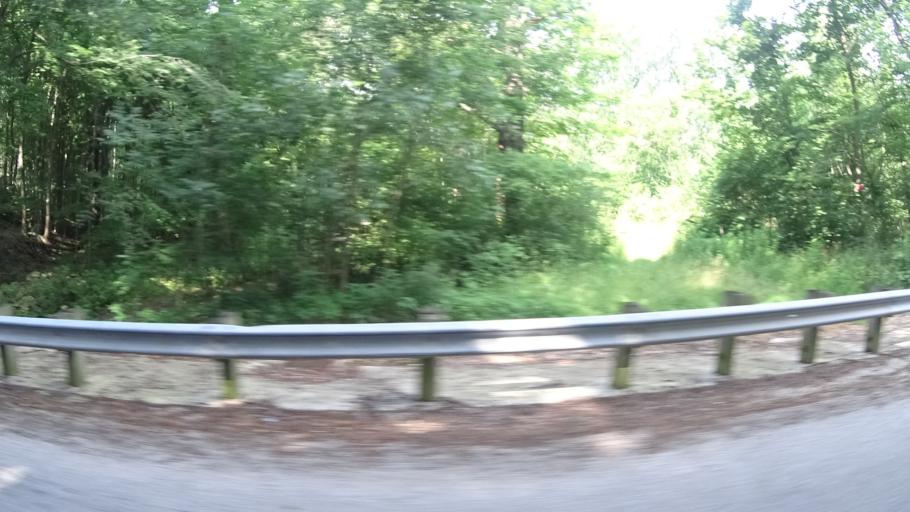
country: US
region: Ohio
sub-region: Lorain County
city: Vermilion
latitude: 41.3949
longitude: -82.4190
